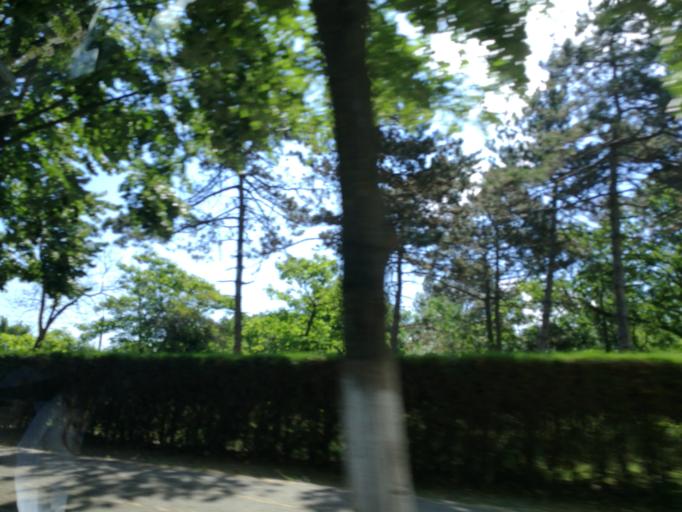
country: RO
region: Constanta
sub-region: Oras Eforie
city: Eforie Nord
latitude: 44.0597
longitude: 28.6354
